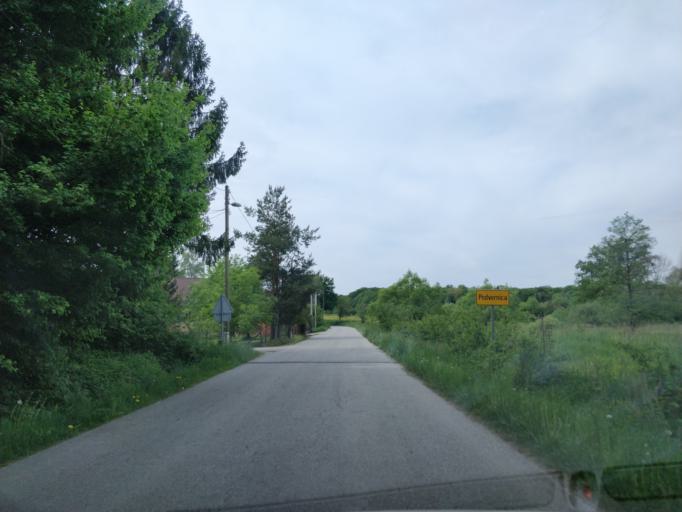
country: HR
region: Zagrebacka
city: Mraclin
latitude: 45.6151
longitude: 16.0780
